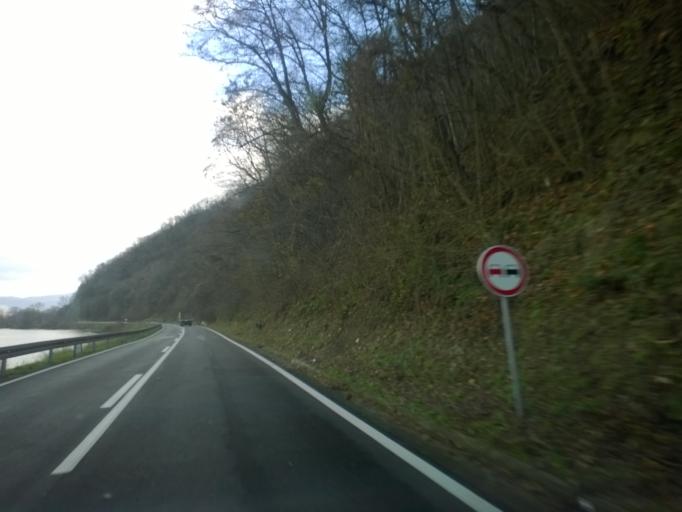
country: RO
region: Caras-Severin
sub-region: Comuna Berzasca
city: Liubcova
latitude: 44.6446
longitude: 21.8295
